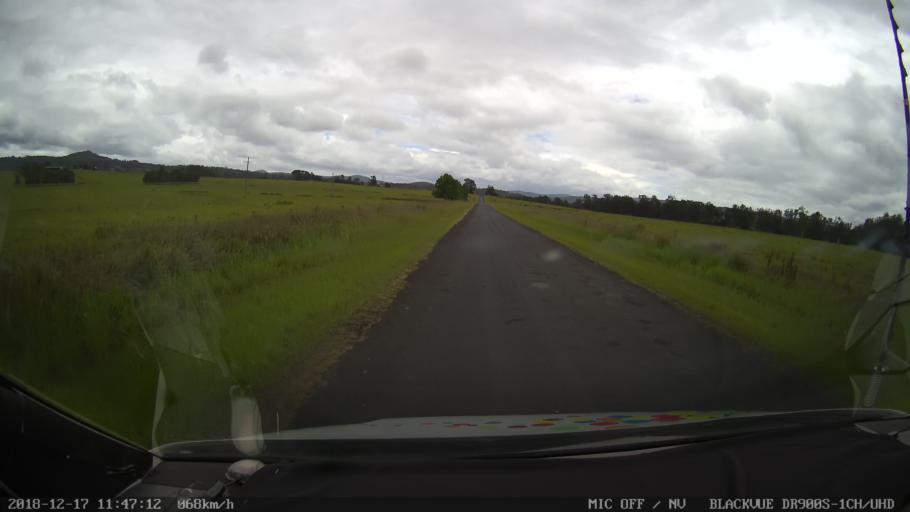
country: AU
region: New South Wales
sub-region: Kyogle
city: Kyogle
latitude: -28.6296
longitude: 152.5918
